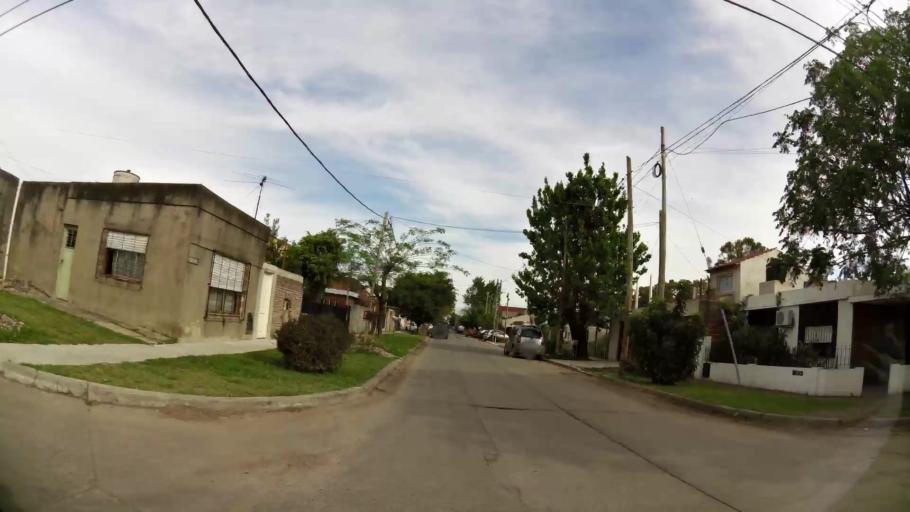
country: AR
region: Buenos Aires
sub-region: Partido de Quilmes
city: Quilmes
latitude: -34.7557
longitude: -58.2738
